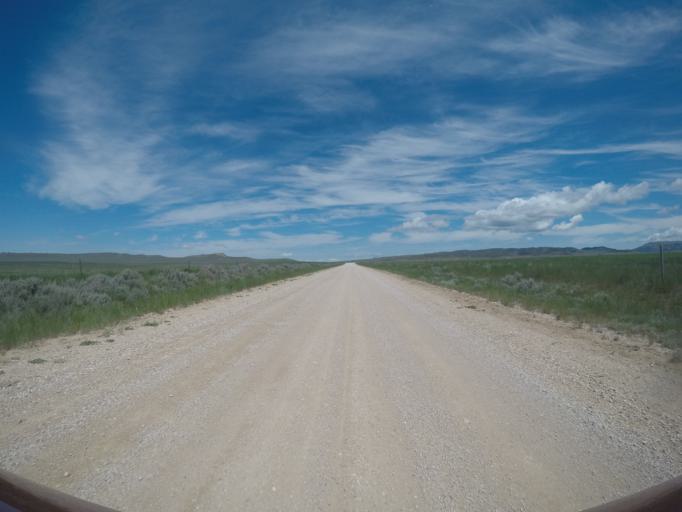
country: US
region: Montana
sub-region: Yellowstone County
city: Laurel
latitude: 45.2170
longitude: -108.7190
